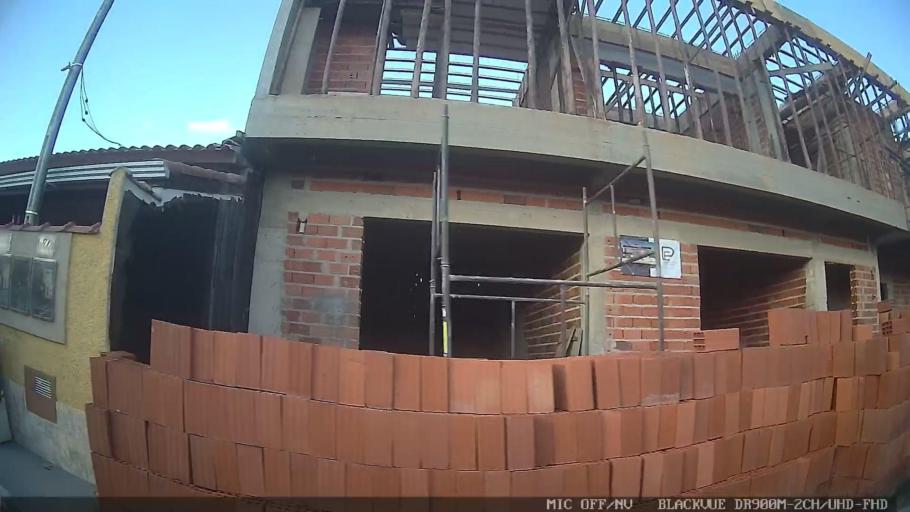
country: BR
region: Minas Gerais
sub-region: Extrema
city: Extrema
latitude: -22.8888
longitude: -46.4152
